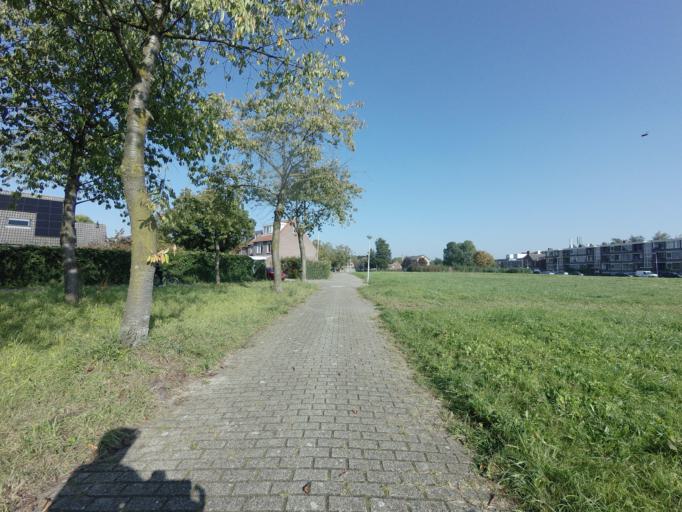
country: NL
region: Gelderland
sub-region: Gemeente Culemborg
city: Culemborg
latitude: 51.9503
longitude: 5.2171
